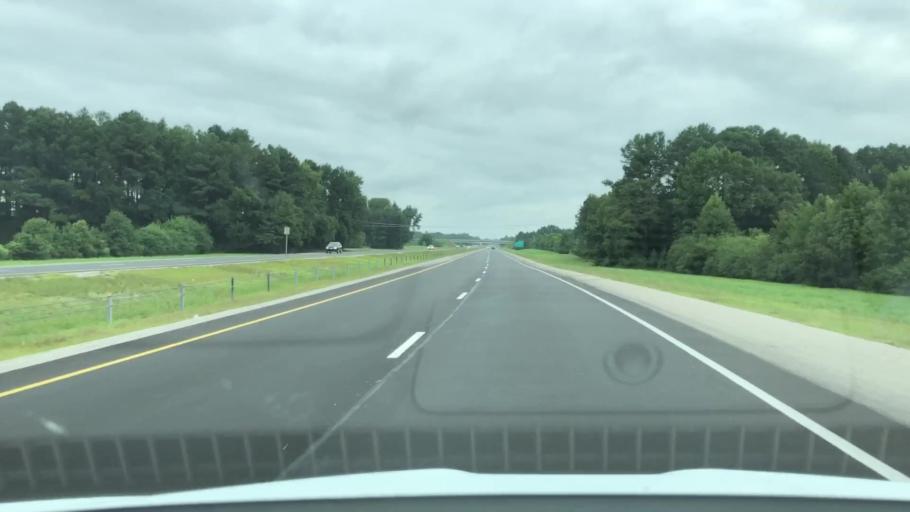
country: US
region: North Carolina
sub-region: Wayne County
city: Fremont
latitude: 35.5976
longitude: -77.9810
